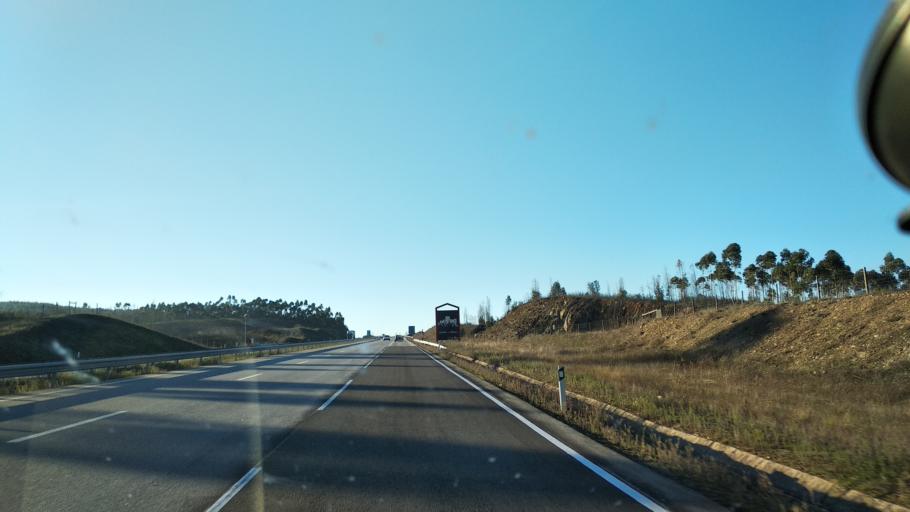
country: PT
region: Portalegre
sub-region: Gaviao
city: Gaviao
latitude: 39.5344
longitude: -7.9118
